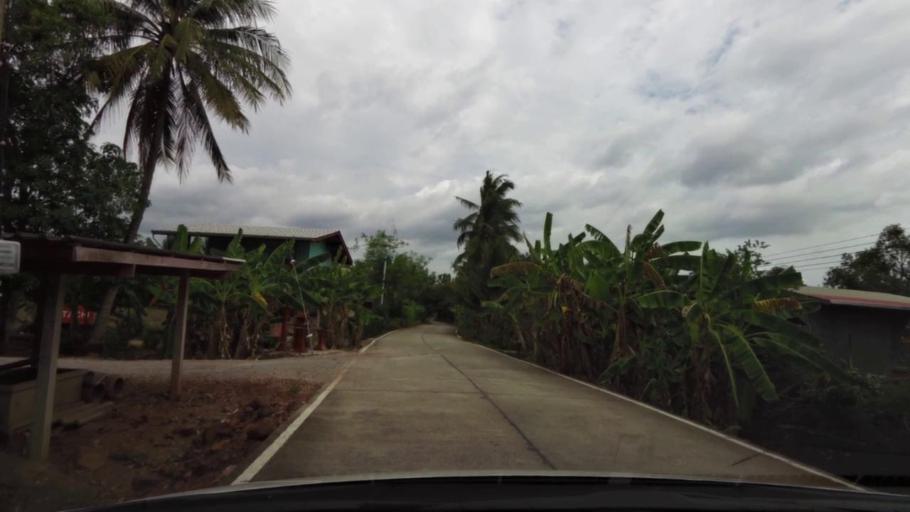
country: TH
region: Ratchaburi
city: Damnoen Saduak
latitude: 13.5513
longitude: 99.9852
